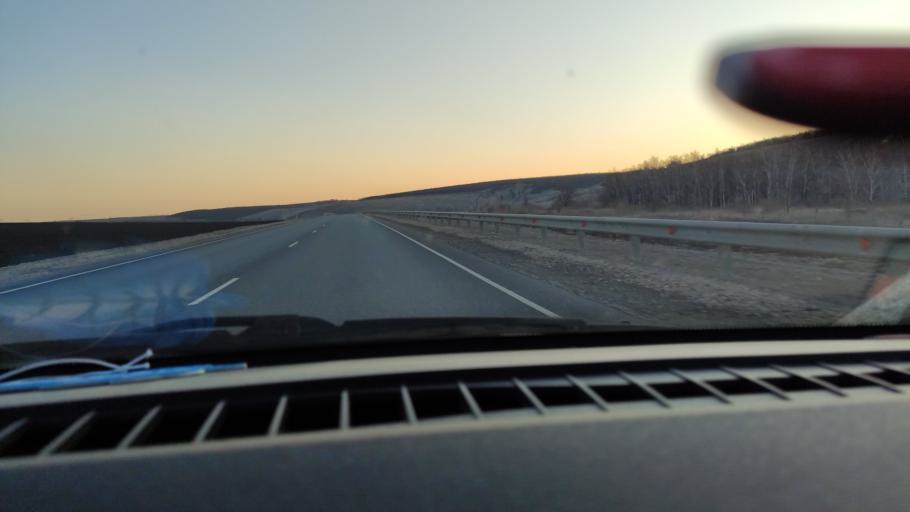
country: RU
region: Saratov
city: Yelshanka
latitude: 51.8599
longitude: 46.4978
